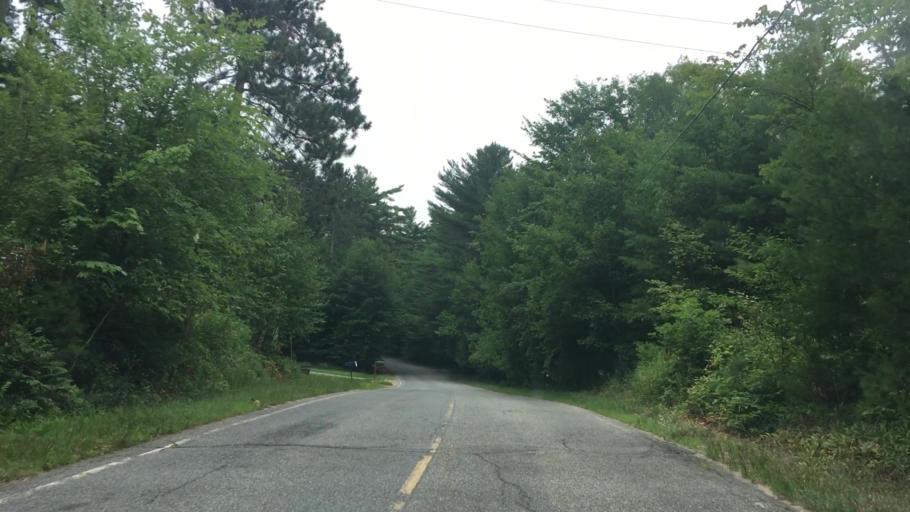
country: US
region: New York
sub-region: Essex County
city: Keeseville
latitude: 44.4153
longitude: -73.6450
